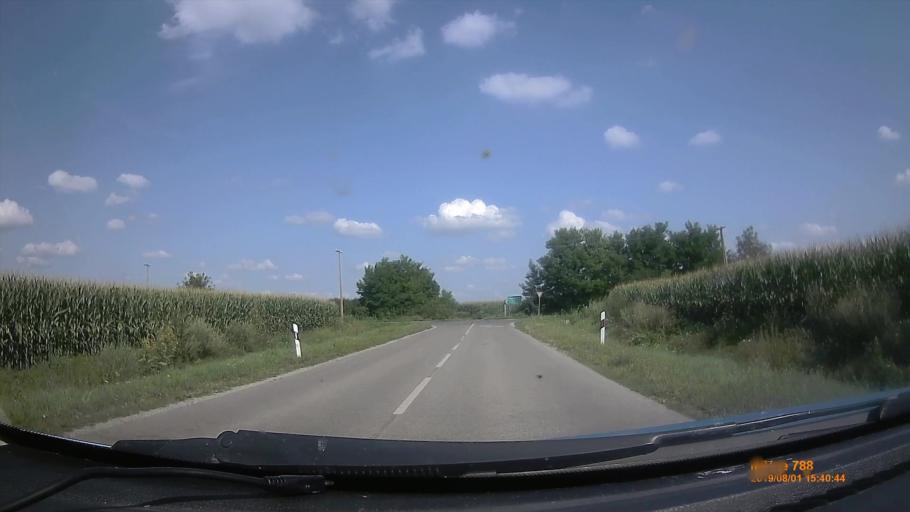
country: HU
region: Baranya
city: Szentlorinc
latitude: 45.9871
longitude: 17.9574
